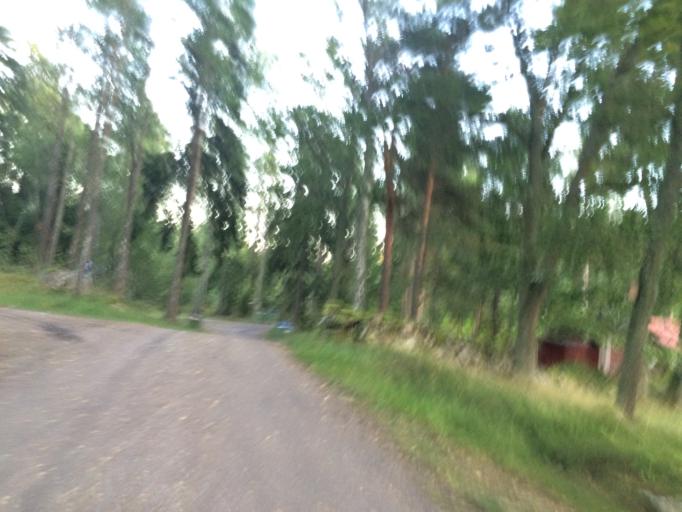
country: SE
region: Soedermanland
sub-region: Eskilstuna Kommun
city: Kvicksund
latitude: 59.4522
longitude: 16.3562
